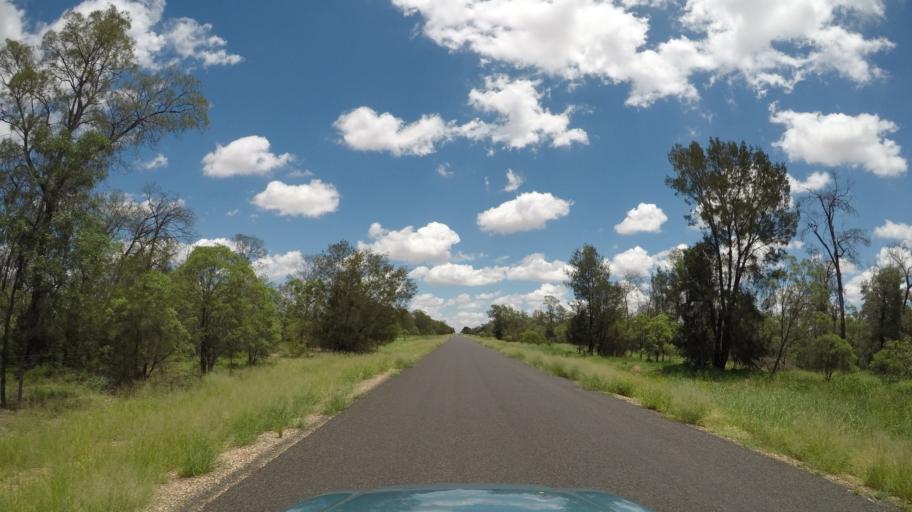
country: AU
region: Queensland
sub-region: Goondiwindi
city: Goondiwindi
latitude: -28.1691
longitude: 150.2028
